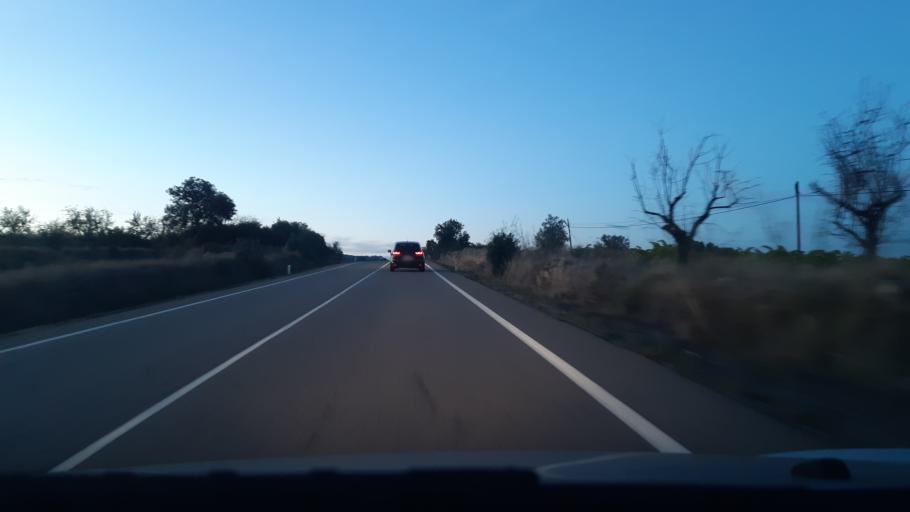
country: ES
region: Aragon
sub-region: Provincia de Teruel
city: Calaceite
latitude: 40.9905
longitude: 0.1987
